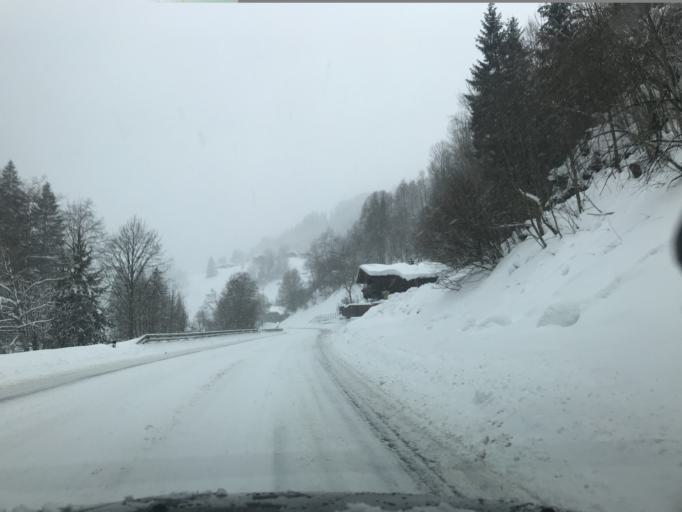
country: AT
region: Salzburg
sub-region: Politischer Bezirk Zell am See
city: Maishofen
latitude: 47.3653
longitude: 12.7671
